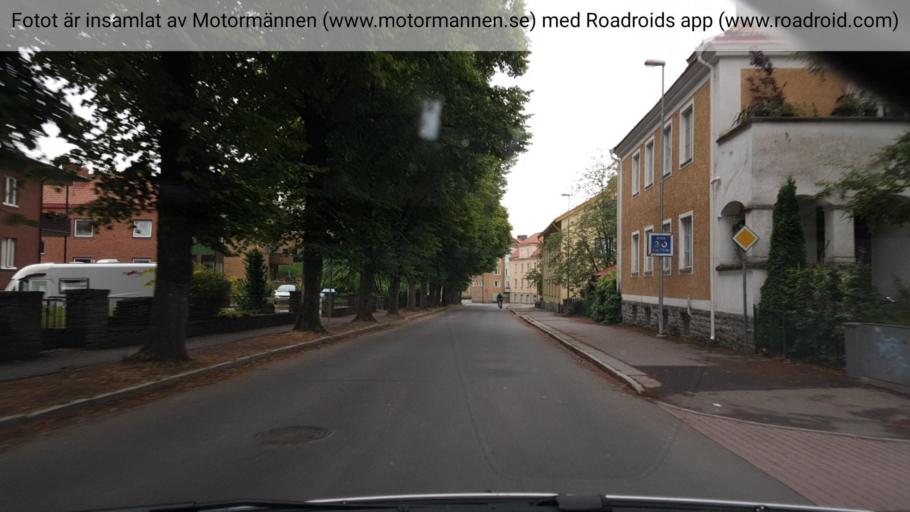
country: SE
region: Vaestra Goetaland
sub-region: Skovde Kommun
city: Skoevde
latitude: 58.3888
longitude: 13.8367
